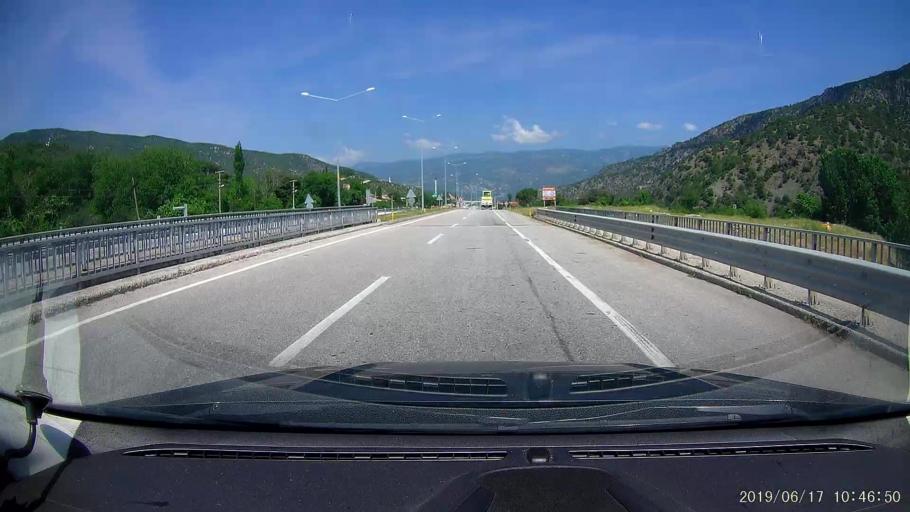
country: TR
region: Corum
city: Hacihamza
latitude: 41.0719
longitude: 34.4568
